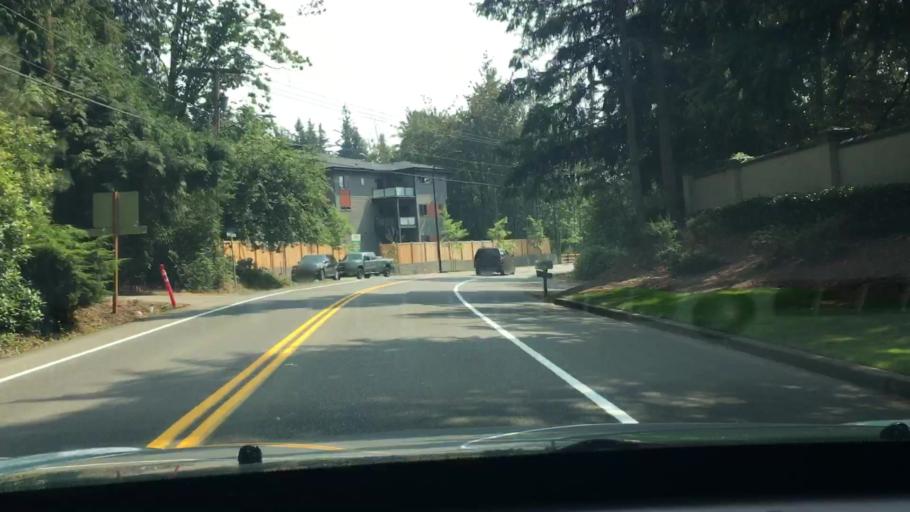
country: US
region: Washington
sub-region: King County
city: City of Sammamish
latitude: 47.6059
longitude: -122.0575
